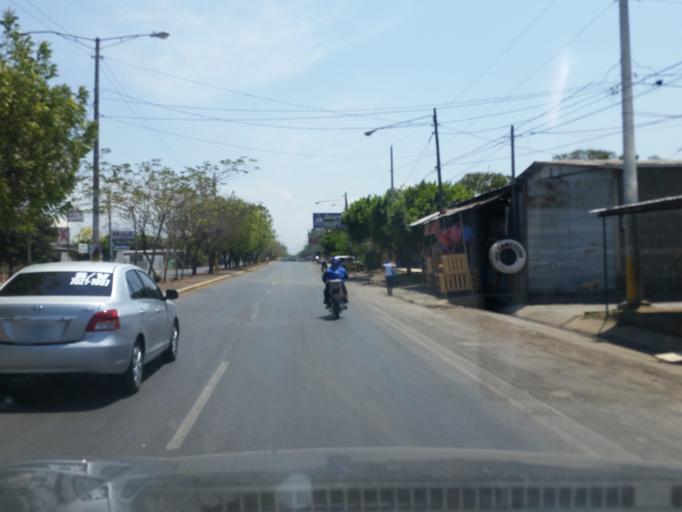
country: NI
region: Managua
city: Tipitapa
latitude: 12.1984
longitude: -86.1035
